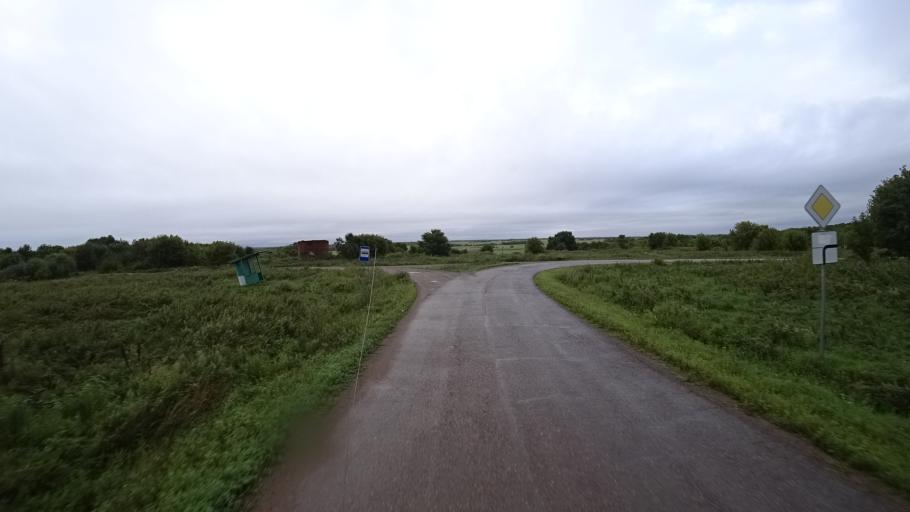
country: RU
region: Primorskiy
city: Monastyrishche
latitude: 44.2762
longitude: 132.4244
